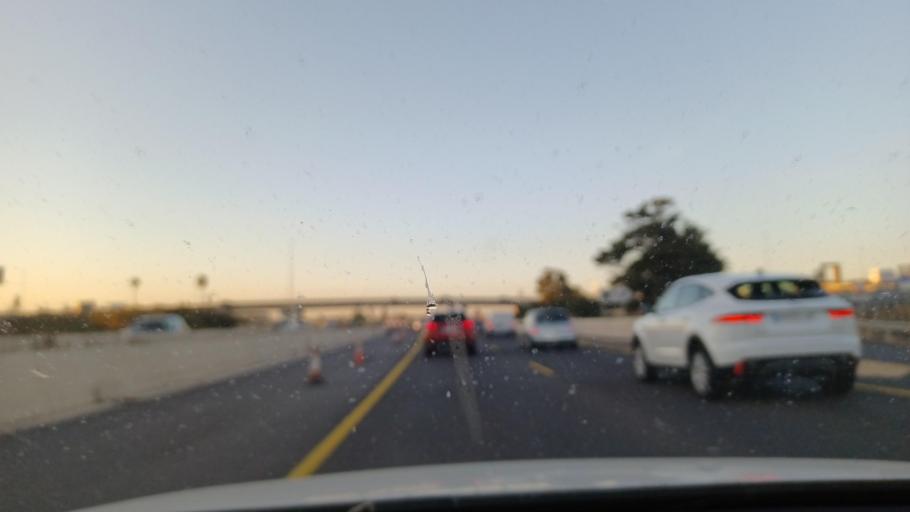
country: ES
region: Valencia
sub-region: Provincia de Valencia
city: Meliana
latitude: 39.5085
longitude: -0.3223
